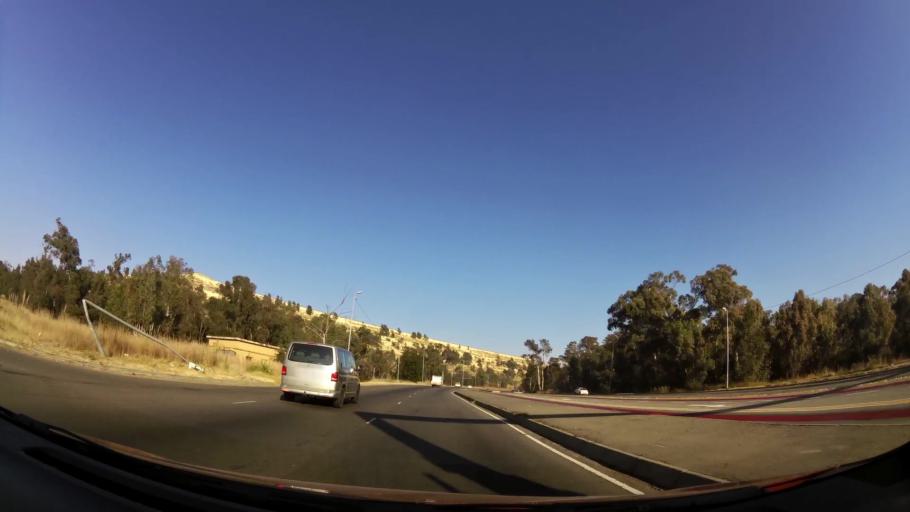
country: ZA
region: Gauteng
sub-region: City of Johannesburg Metropolitan Municipality
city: Johannesburg
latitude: -26.2337
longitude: 27.9748
